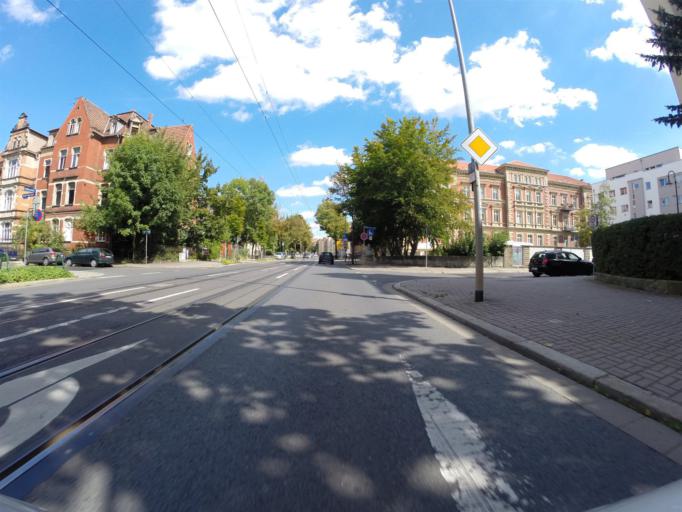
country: DE
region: Thuringia
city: Erfurt
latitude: 50.9675
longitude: 11.0289
